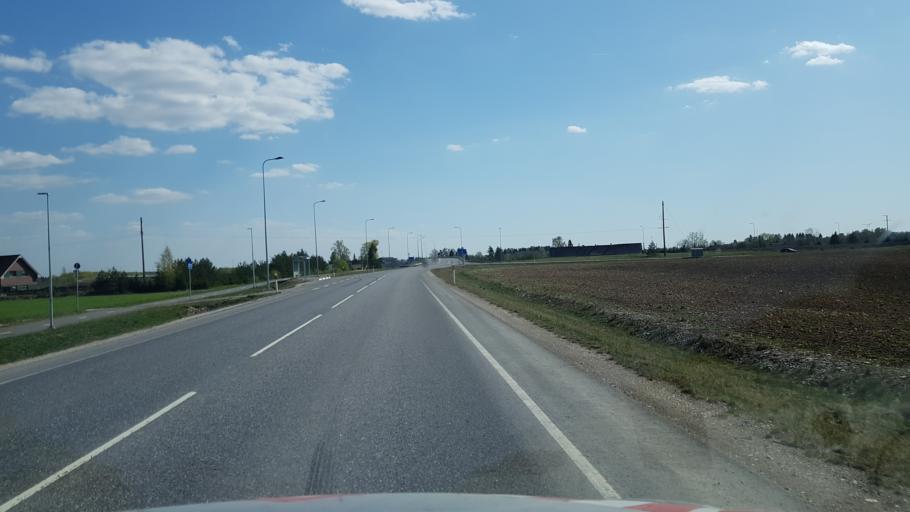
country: EE
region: Harju
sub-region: Raasiku vald
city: Arukula
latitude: 59.1869
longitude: 25.1151
